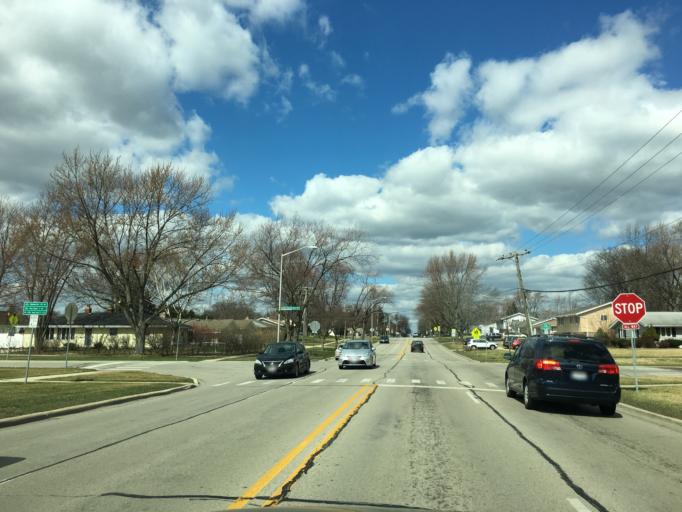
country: US
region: Illinois
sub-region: DuPage County
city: Hanover Park
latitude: 42.0181
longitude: -88.1192
